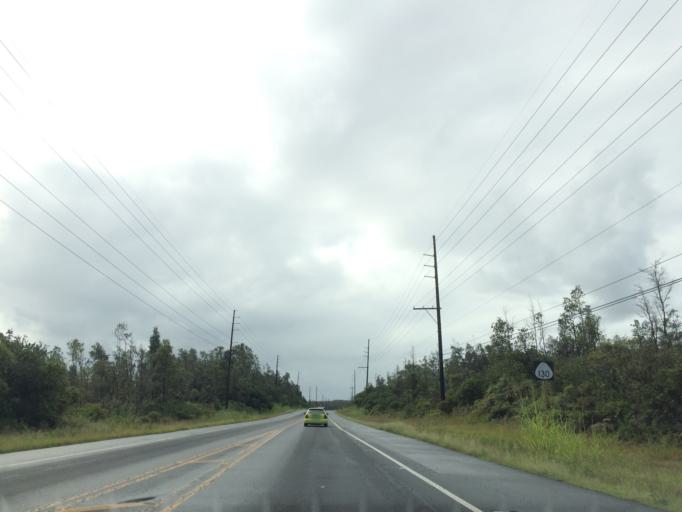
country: US
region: Hawaii
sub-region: Hawaii County
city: Ainaloa
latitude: 19.5347
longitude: -154.9721
